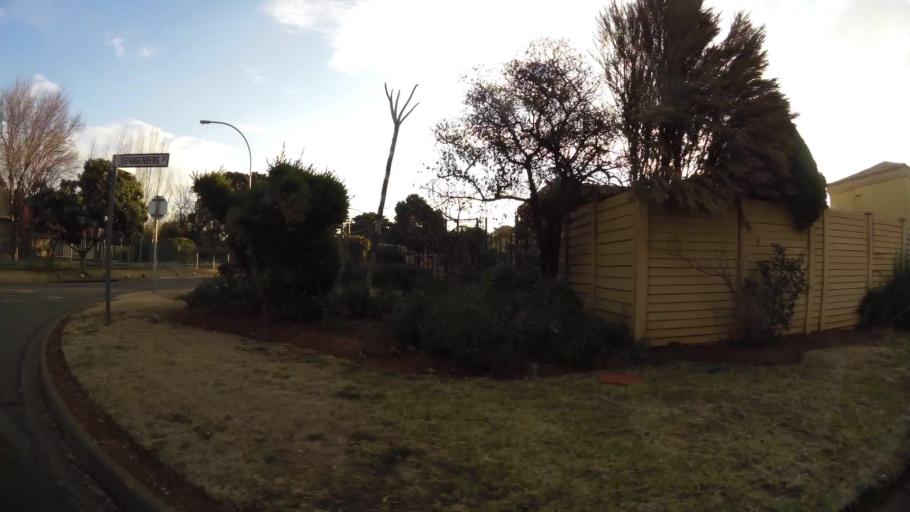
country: ZA
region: Orange Free State
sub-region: Mangaung Metropolitan Municipality
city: Bloemfontein
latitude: -29.1384
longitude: 26.1788
